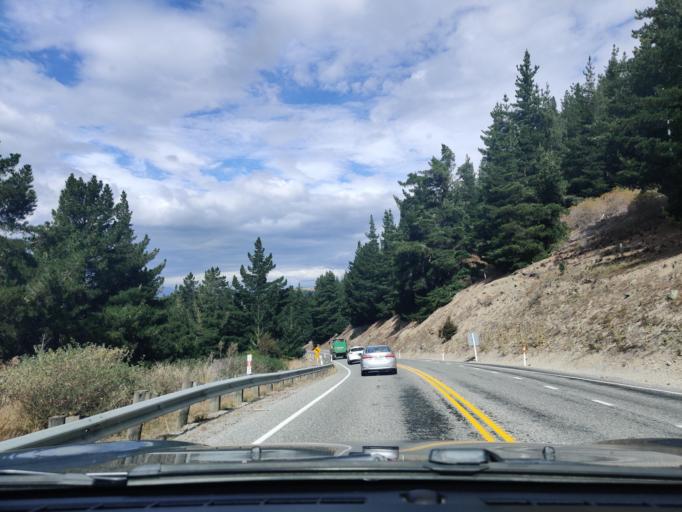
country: NZ
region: Otago
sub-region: Queenstown-Lakes District
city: Wanaka
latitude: -44.7308
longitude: 169.2540
